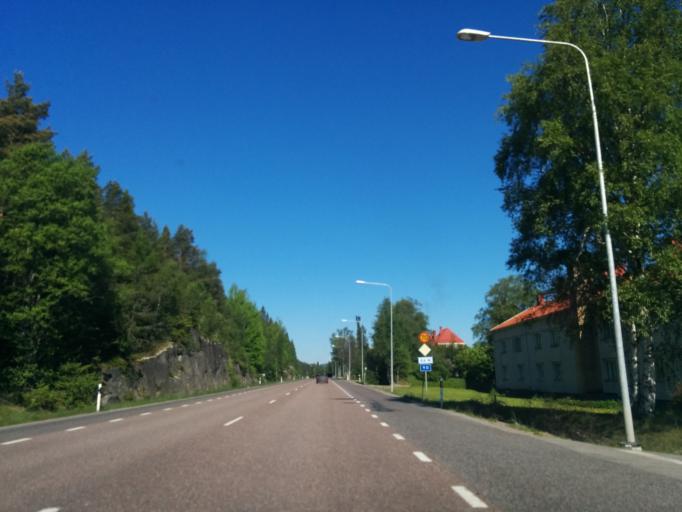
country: SE
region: Vaesternorrland
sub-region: Kramfors Kommun
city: Kramfors
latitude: 62.9075
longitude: 17.8190
